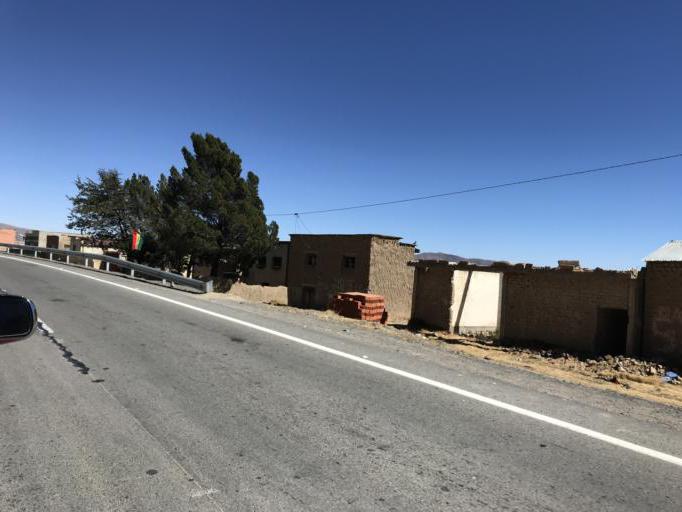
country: BO
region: La Paz
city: Batallas
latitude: -16.2499
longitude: -68.5694
